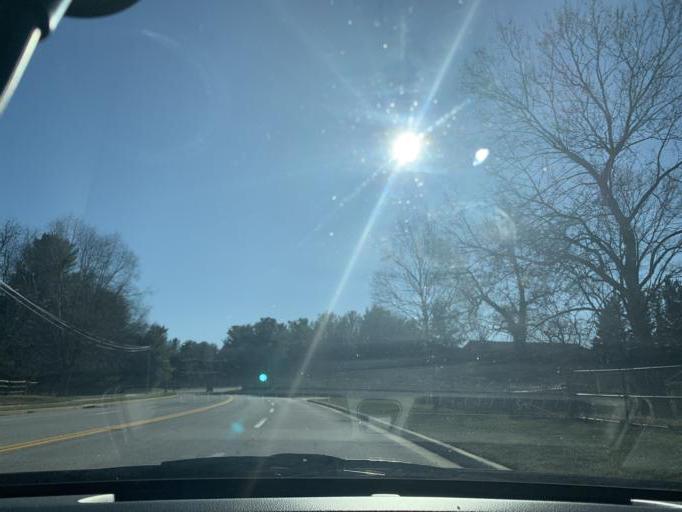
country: US
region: Maryland
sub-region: Baltimore County
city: Garrison
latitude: 39.4020
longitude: -76.7481
